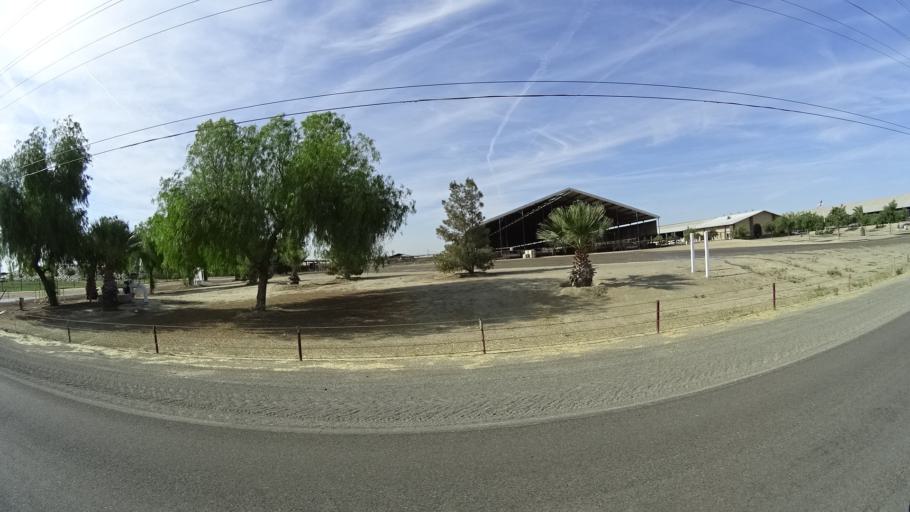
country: US
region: California
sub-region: Tulare County
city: Goshen
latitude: 36.3427
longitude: -119.5140
